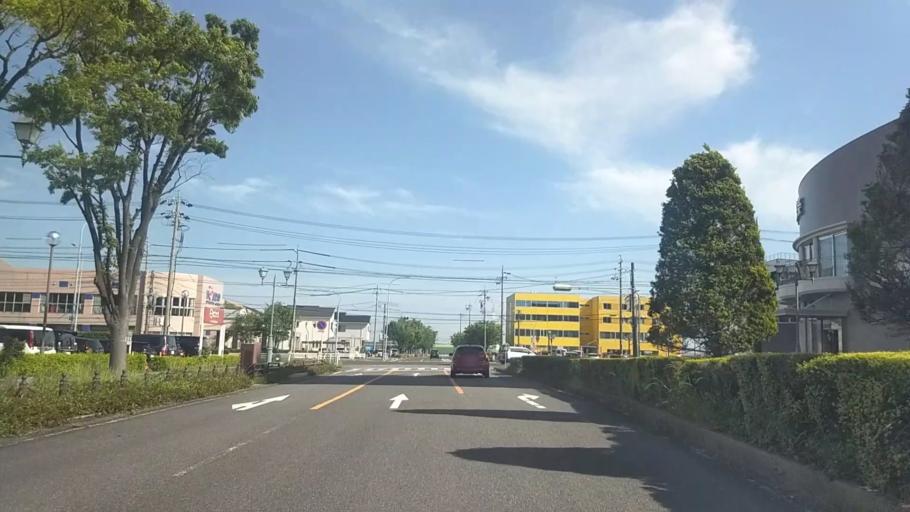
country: JP
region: Aichi
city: Anjo
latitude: 34.9649
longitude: 137.0616
